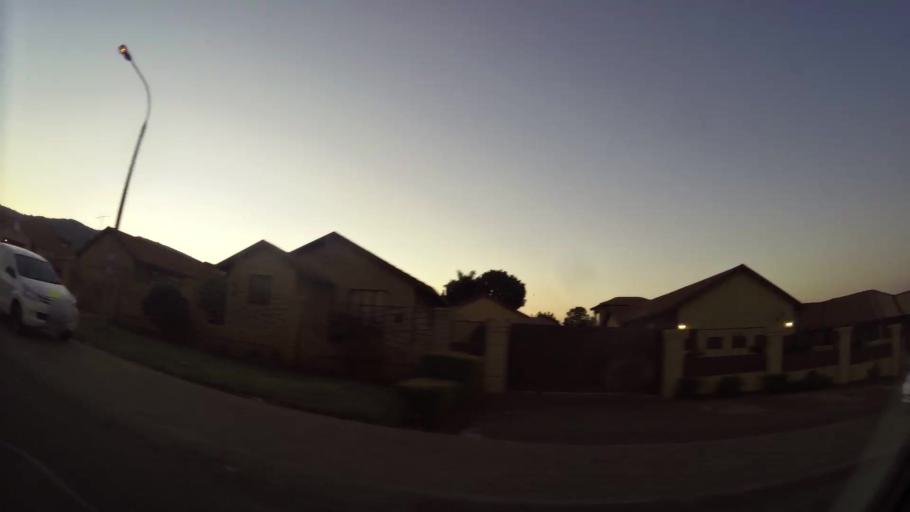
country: ZA
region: North-West
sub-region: Bojanala Platinum District Municipality
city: Rustenburg
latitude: -25.6564
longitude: 27.2081
